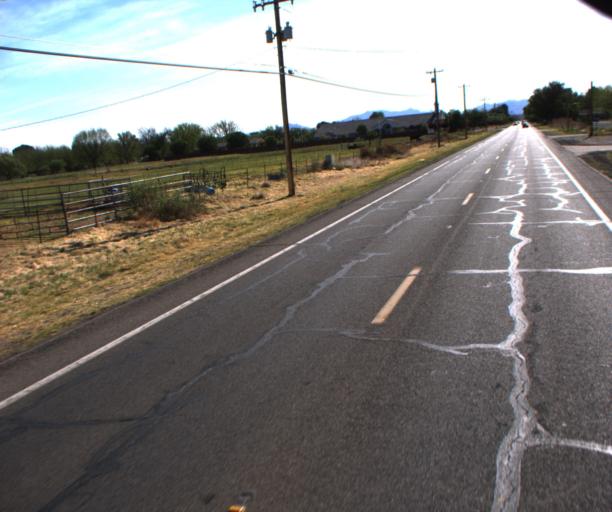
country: US
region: Arizona
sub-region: Cochise County
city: Saint David
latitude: 31.9053
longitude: -110.2390
